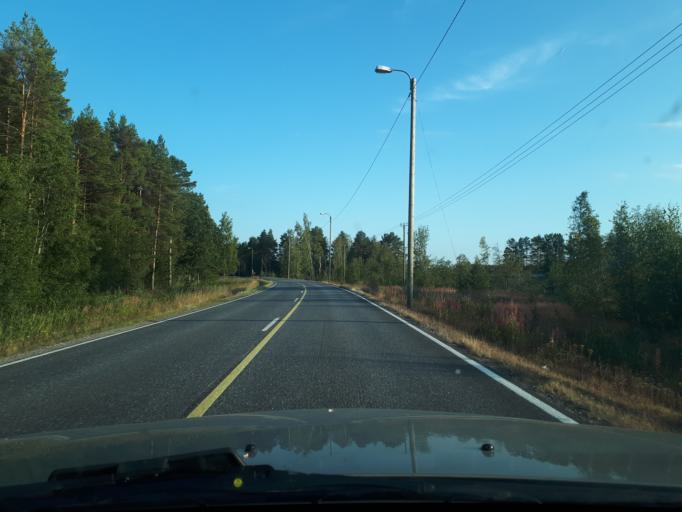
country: FI
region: Northern Ostrobothnia
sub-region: Oulu
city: Oulunsalo
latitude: 64.9897
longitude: 25.2576
